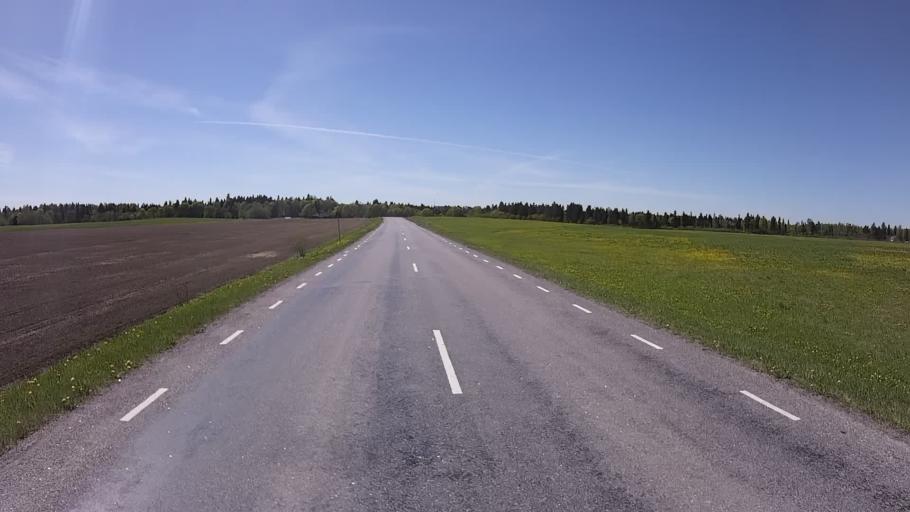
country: EE
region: Harju
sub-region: Rae vald
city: Vaida
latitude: 59.0634
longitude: 25.1488
